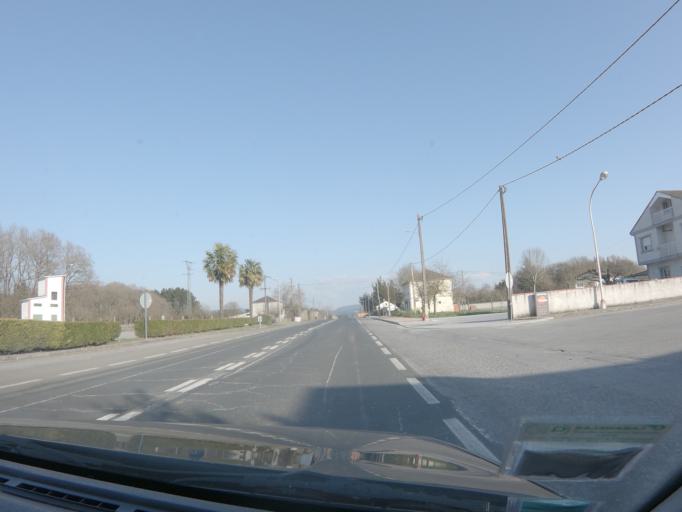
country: ES
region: Galicia
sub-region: Provincia de Lugo
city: Corgo
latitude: 42.9448
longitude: -7.4364
